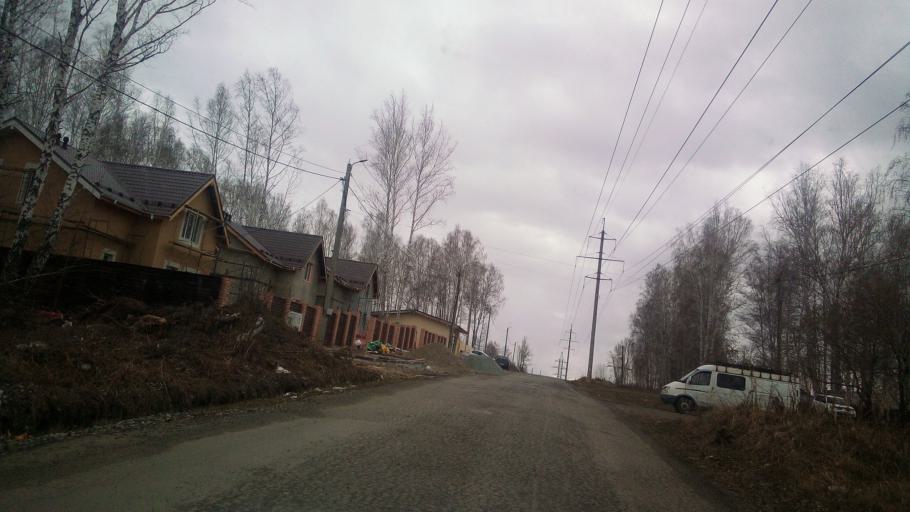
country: RU
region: Chelyabinsk
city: Sargazy
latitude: 55.1316
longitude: 61.2435
